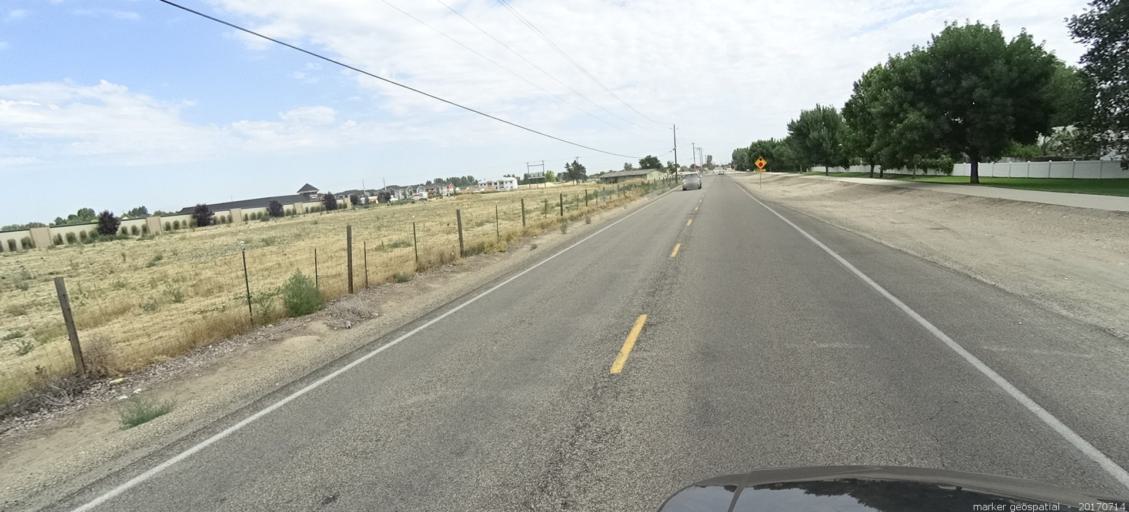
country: US
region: Idaho
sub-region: Ada County
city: Kuna
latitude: 43.5008
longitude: -116.4337
